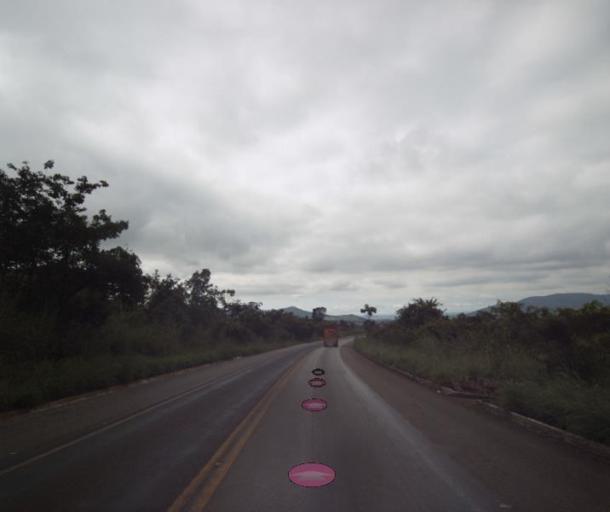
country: BR
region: Goias
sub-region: Barro Alto
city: Barro Alto
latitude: -14.9393
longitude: -48.9403
